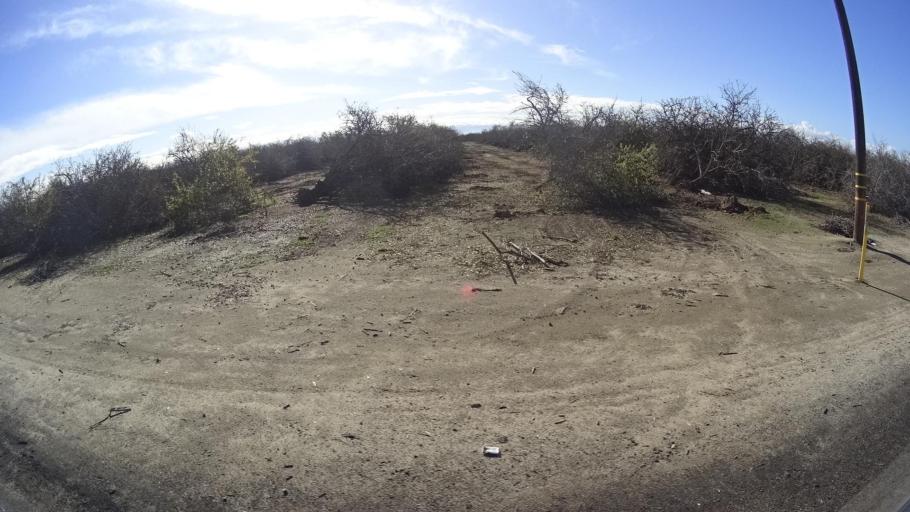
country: US
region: California
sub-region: Kern County
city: Rosedale
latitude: 35.3689
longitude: -119.2325
